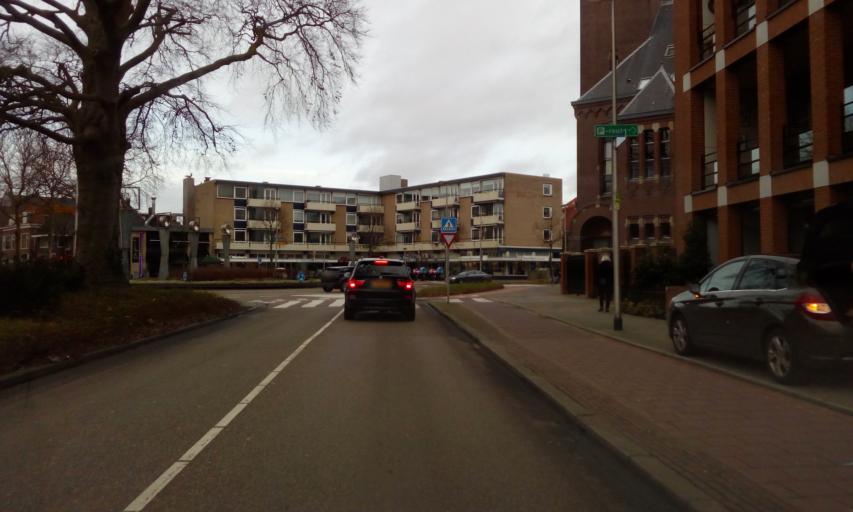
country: NL
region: North Holland
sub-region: Gemeente Bussum
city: Bussum
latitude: 52.2733
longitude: 5.1663
